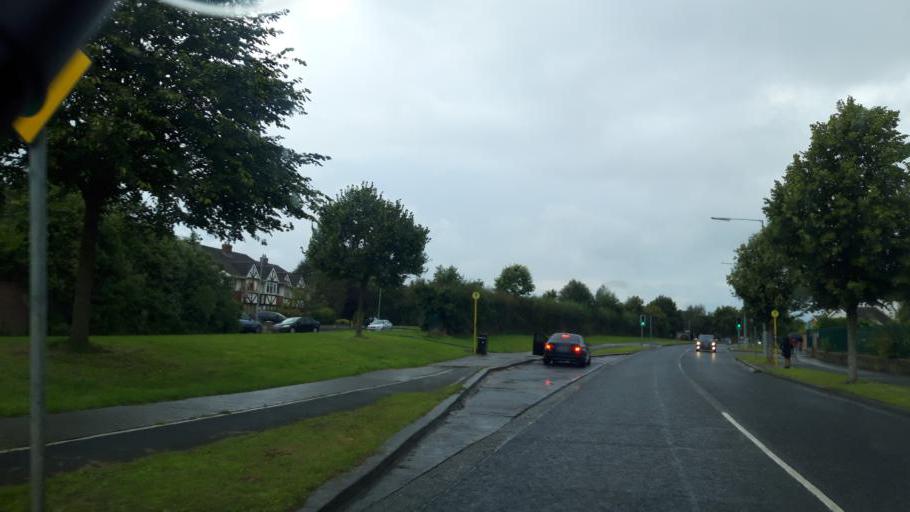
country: IE
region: Leinster
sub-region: Fingal County
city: Blanchardstown
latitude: 53.3701
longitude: -6.3922
